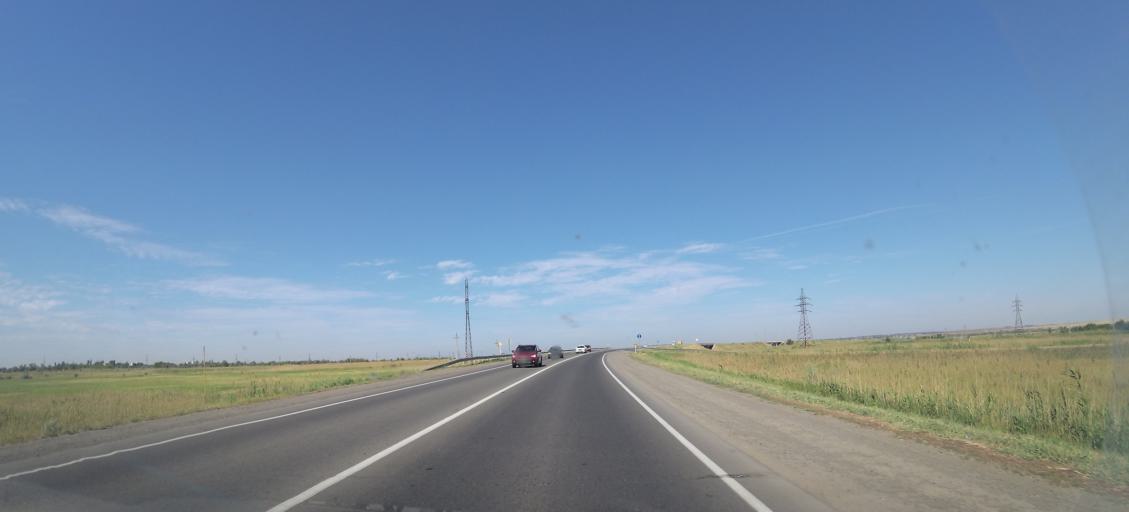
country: RU
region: Volgograd
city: Oktyabr'skiy
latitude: 48.6740
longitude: 43.8807
